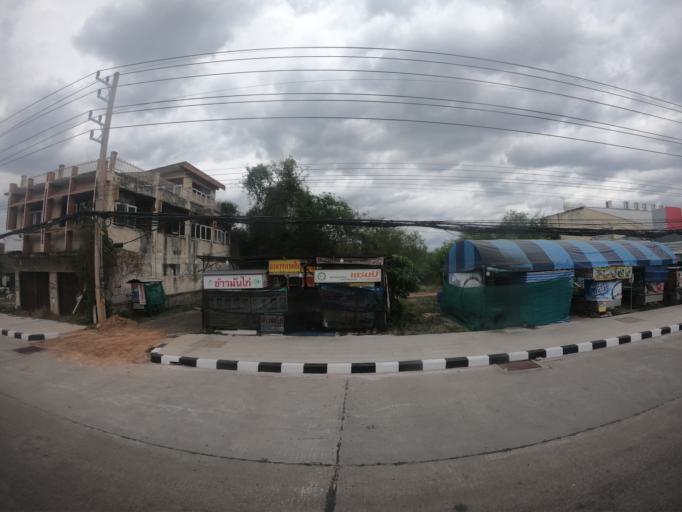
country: TH
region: Nakhon Ratchasima
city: Nakhon Ratchasima
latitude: 14.9546
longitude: 102.1215
